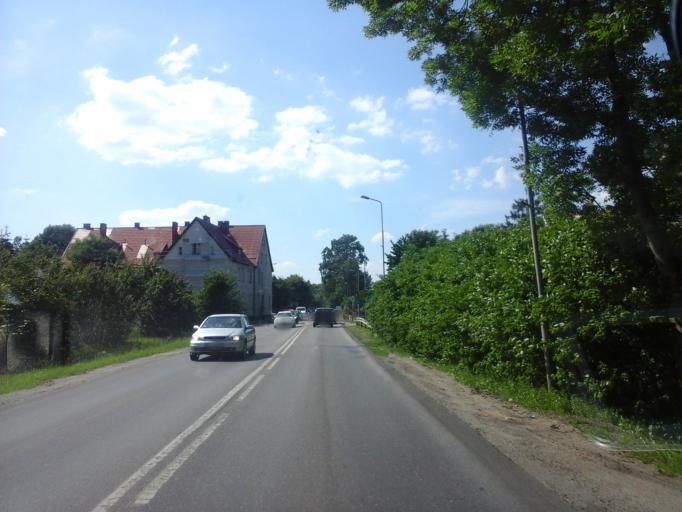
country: PL
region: West Pomeranian Voivodeship
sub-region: Powiat bialogardzki
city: Bialogard
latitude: 54.0036
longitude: 15.9844
